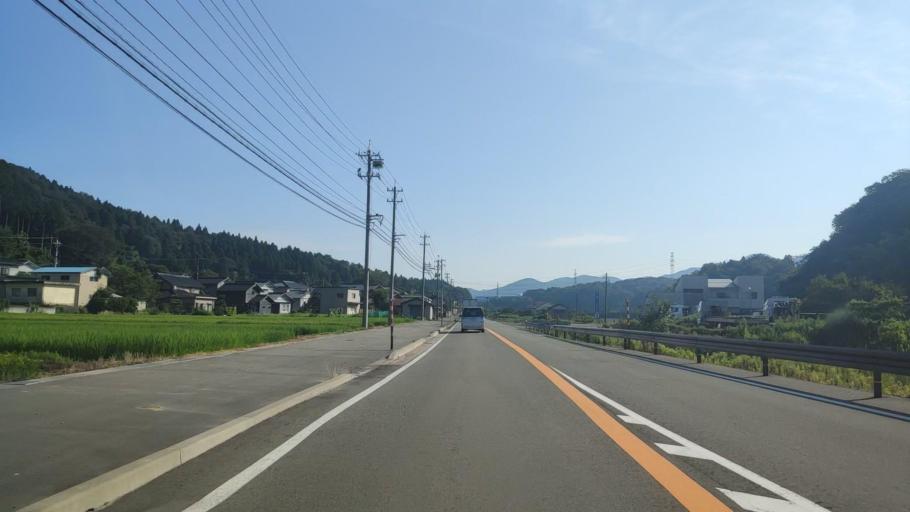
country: JP
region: Fukui
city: Maruoka
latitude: 36.2150
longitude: 136.2727
